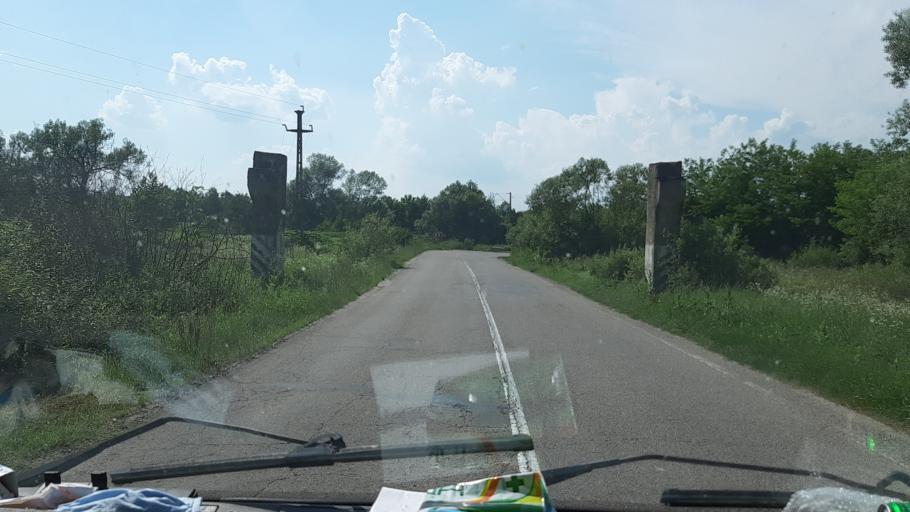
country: RO
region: Caras-Severin
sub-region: Comuna Ezeris
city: Ezeris
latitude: 45.3982
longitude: 21.9158
